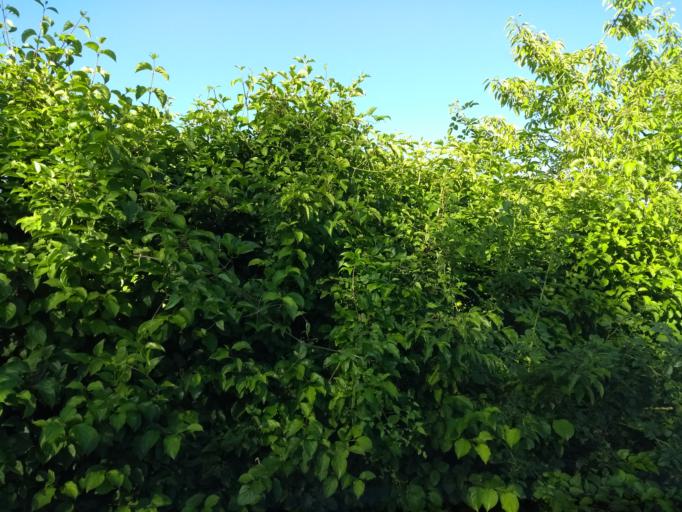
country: DE
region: Bavaria
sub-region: Upper Bavaria
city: Muehldorf
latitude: 48.2406
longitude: 12.5218
